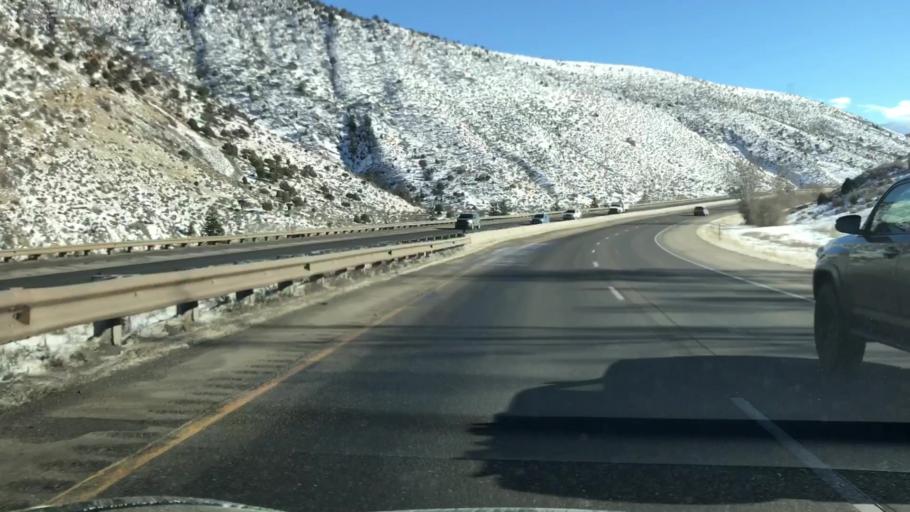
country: US
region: Colorado
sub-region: Eagle County
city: Edwards
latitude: 39.6810
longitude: -106.6494
